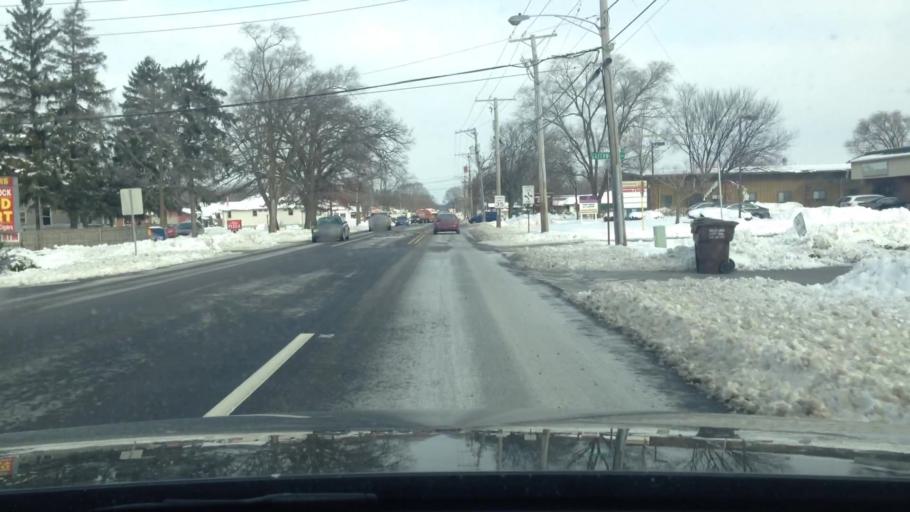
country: US
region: Illinois
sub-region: McHenry County
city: Woodstock
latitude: 42.3250
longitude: -88.4432
